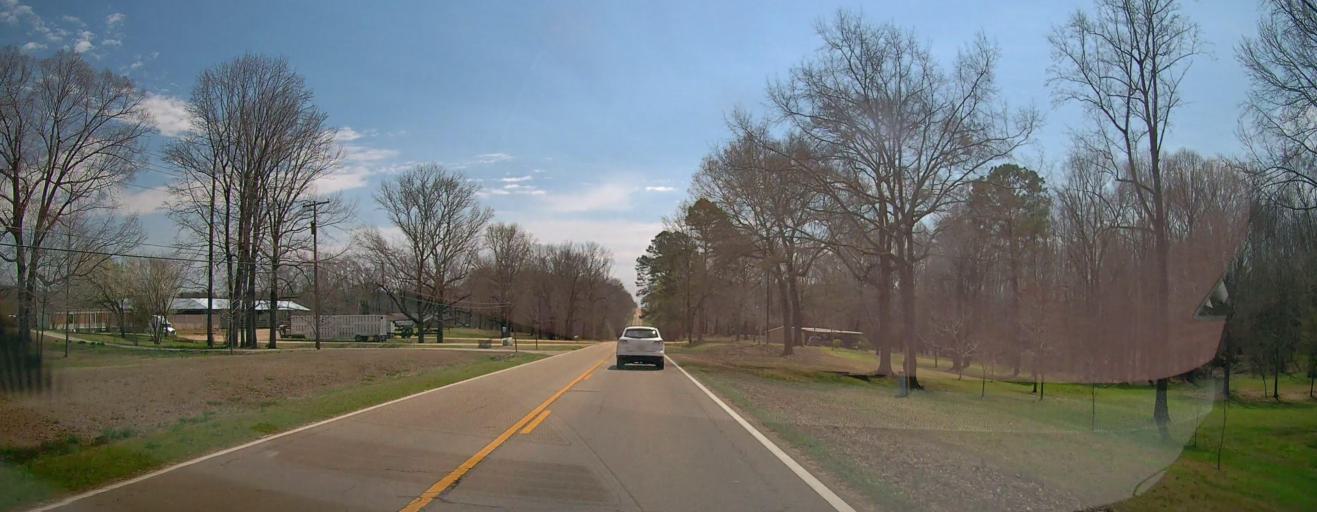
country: US
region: Mississippi
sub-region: Union County
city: New Albany
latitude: 34.4463
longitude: -88.9668
